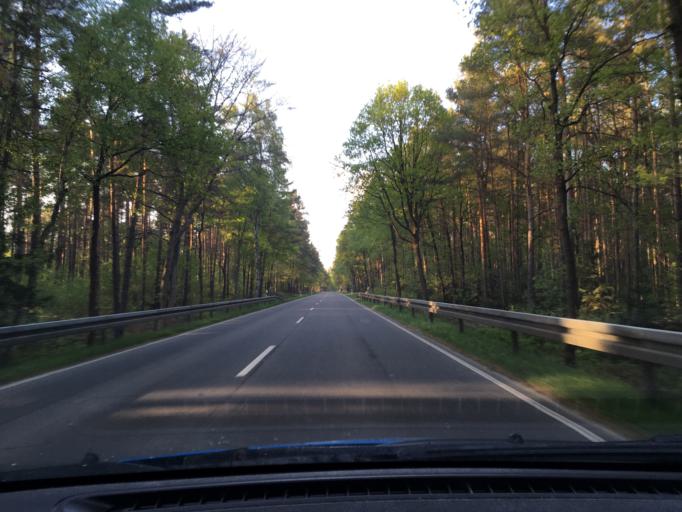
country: DE
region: Lower Saxony
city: Wietzendorf
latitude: 52.8676
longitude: 9.9810
